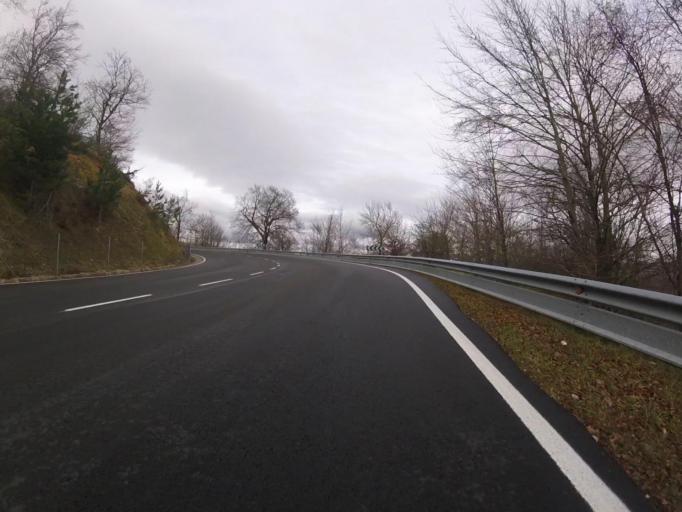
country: ES
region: Navarre
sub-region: Provincia de Navarra
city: Arbizu
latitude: 42.8662
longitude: -2.0229
